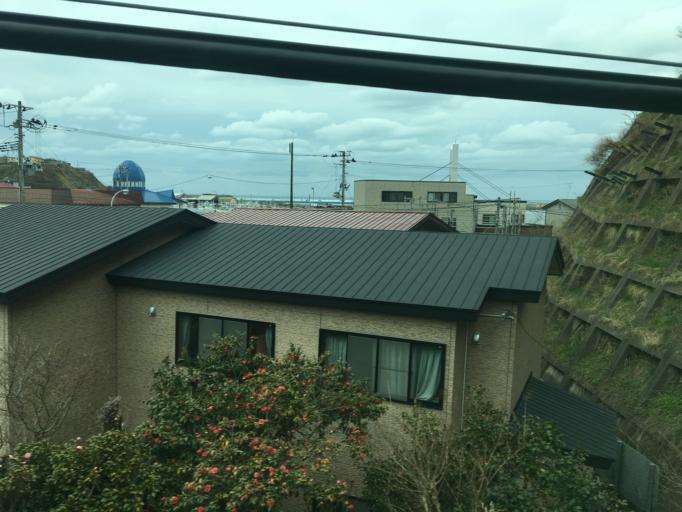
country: JP
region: Akita
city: Noshiromachi
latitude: 40.6416
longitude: 139.9294
